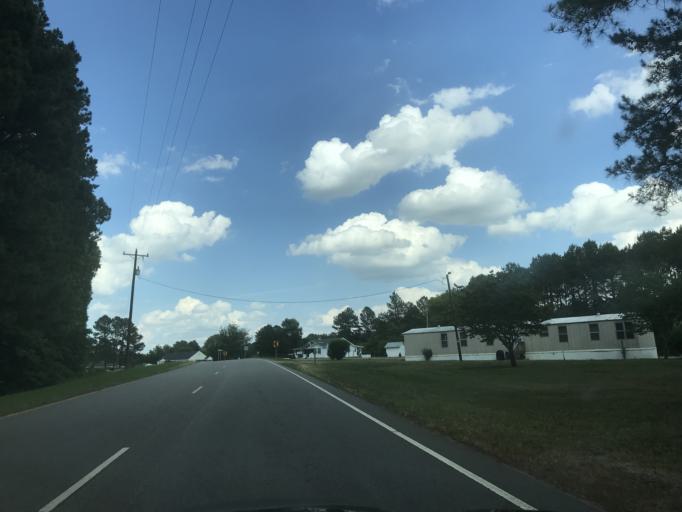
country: US
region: North Carolina
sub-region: Nash County
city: Spring Hope
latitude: 35.9199
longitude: -78.1599
